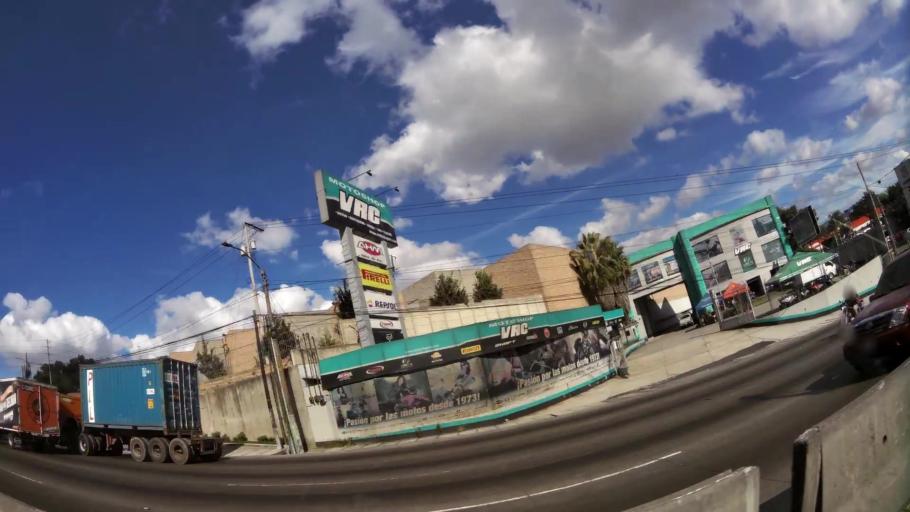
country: GT
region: Guatemala
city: Villa Nueva
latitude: 14.5633
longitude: -90.5760
